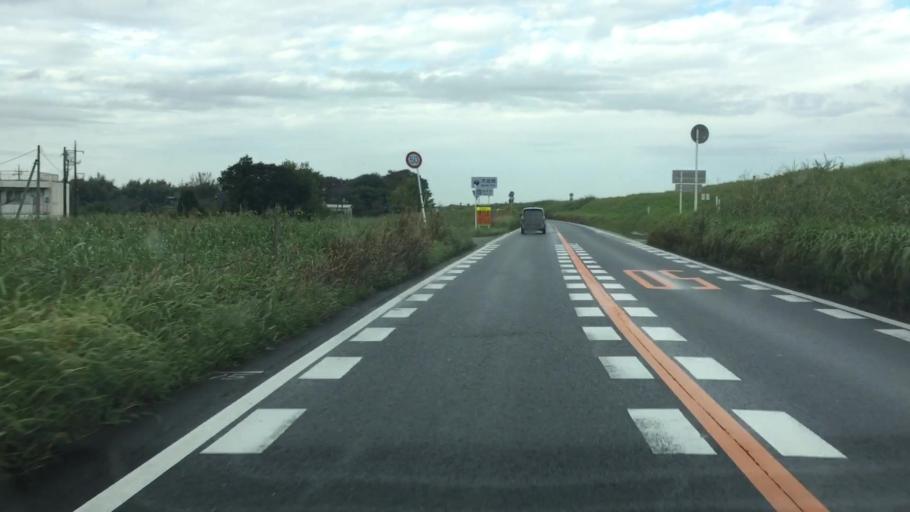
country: JP
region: Ibaraki
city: Toride
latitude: 35.8814
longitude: 140.0835
